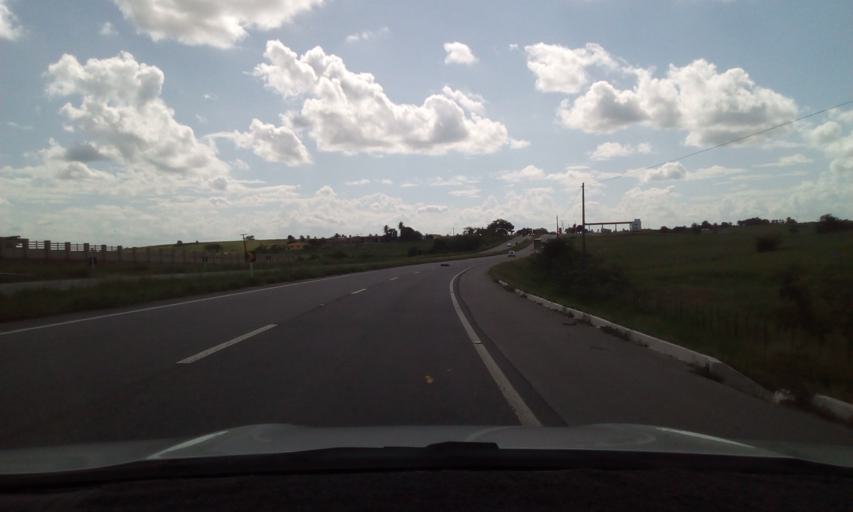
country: BR
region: Paraiba
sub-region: Pilar
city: Pilar
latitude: -7.1909
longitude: -35.2688
